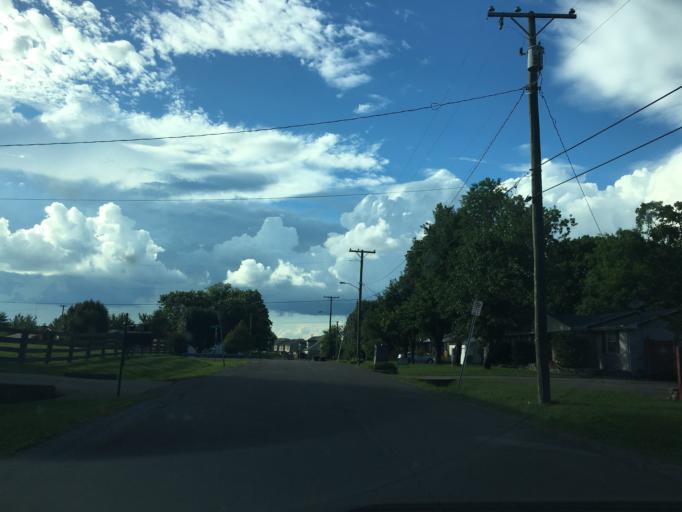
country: US
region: Tennessee
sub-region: Davidson County
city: Oak Hill
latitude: 36.0651
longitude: -86.7194
